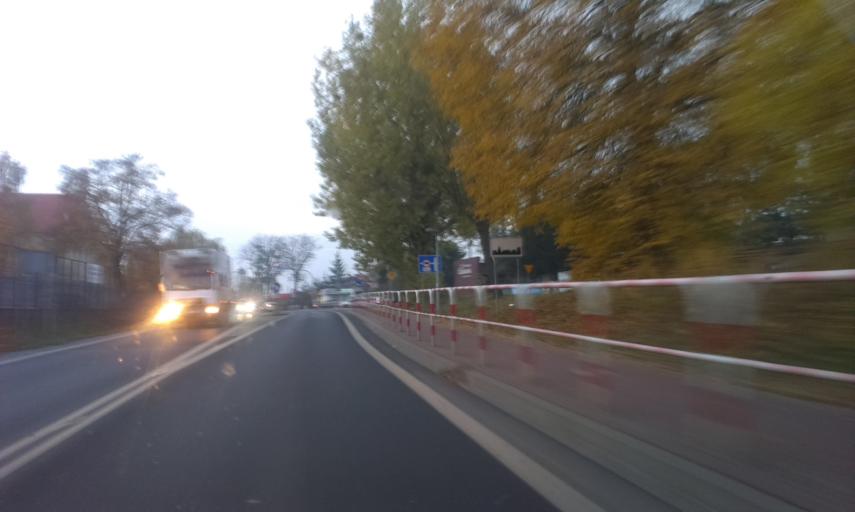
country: PL
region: Greater Poland Voivodeship
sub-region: Powiat obornicki
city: Oborniki
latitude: 52.6309
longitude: 16.8092
